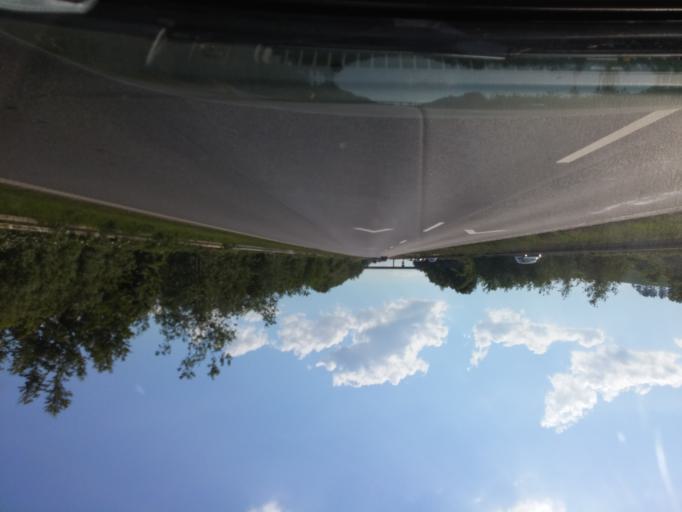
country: DK
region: South Denmark
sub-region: Assens Kommune
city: Vissenbjerg
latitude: 55.4033
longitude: 10.1480
